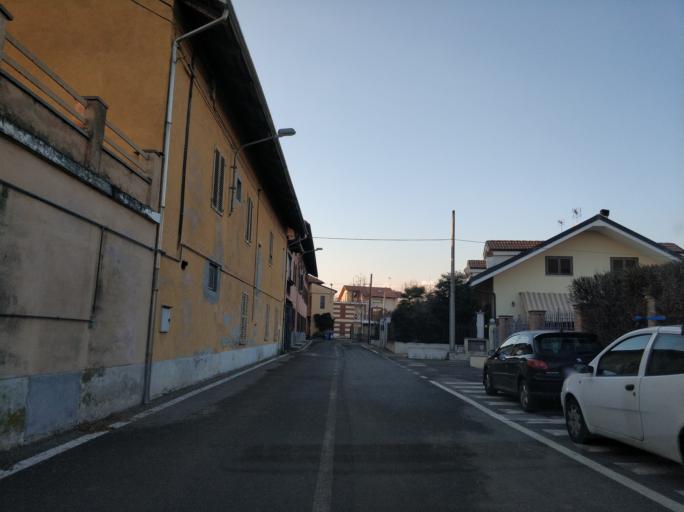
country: IT
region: Piedmont
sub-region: Provincia di Torino
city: San Maurizio
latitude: 45.2219
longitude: 7.6282
